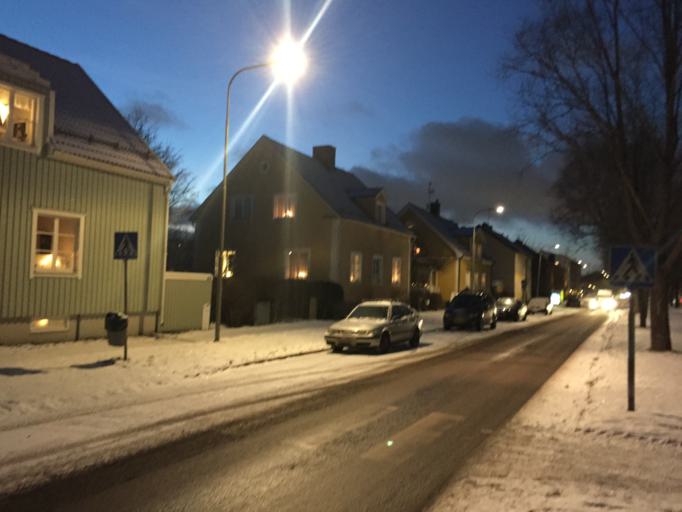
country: SE
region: Stockholm
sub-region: Stockholms Kommun
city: Arsta
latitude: 59.2811
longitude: 18.0806
